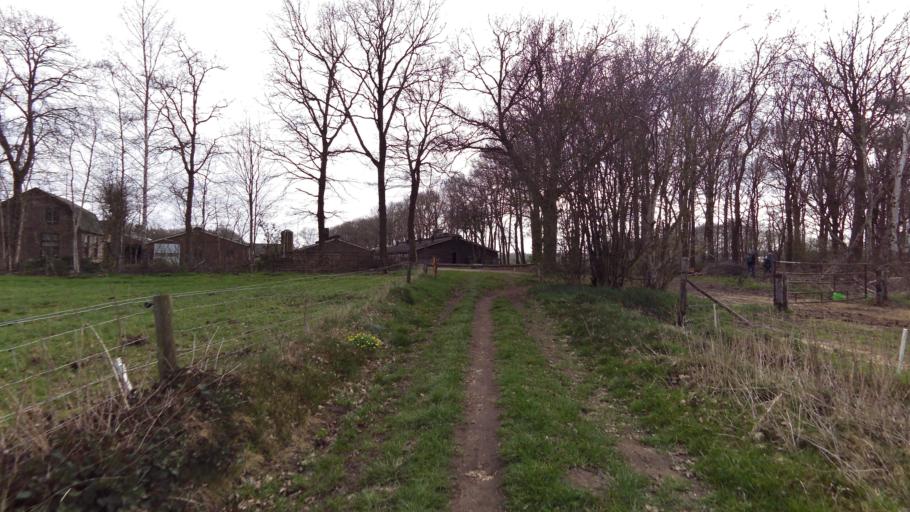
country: NL
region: Gelderland
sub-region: Gemeente Barneveld
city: Voorthuizen
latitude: 52.2010
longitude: 5.5929
